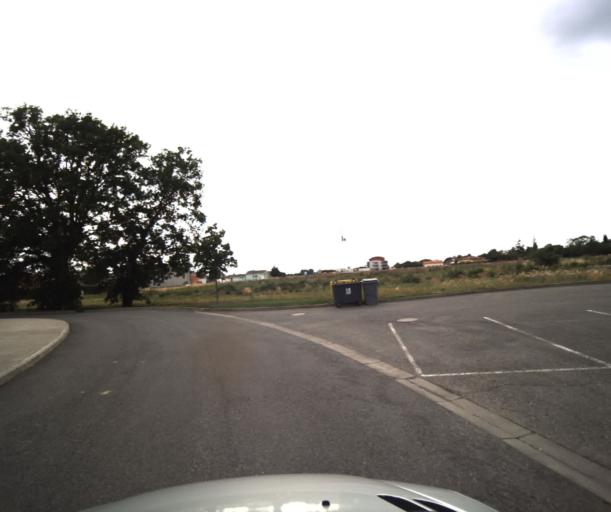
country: FR
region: Midi-Pyrenees
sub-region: Departement de la Haute-Garonne
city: Labarthe-sur-Leze
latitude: 43.4539
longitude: 1.3979
